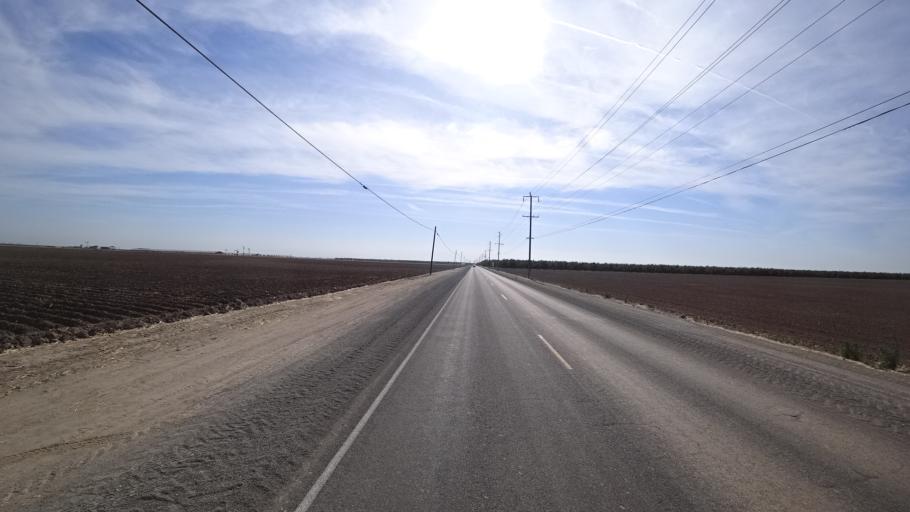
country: US
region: California
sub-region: Tulare County
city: Goshen
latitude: 36.3427
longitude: -119.5101
